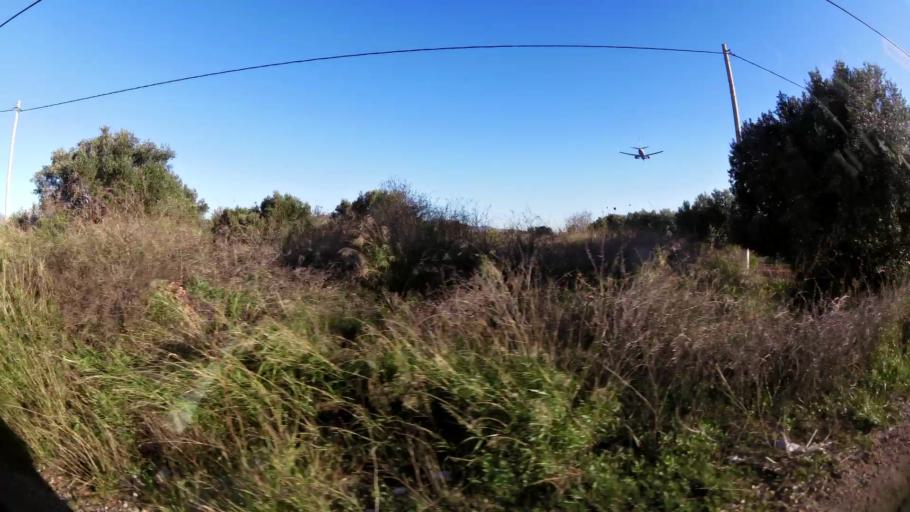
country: GR
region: Attica
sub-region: Nomarchia Anatolikis Attikis
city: Markopoulo
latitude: 37.9143
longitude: 23.9122
